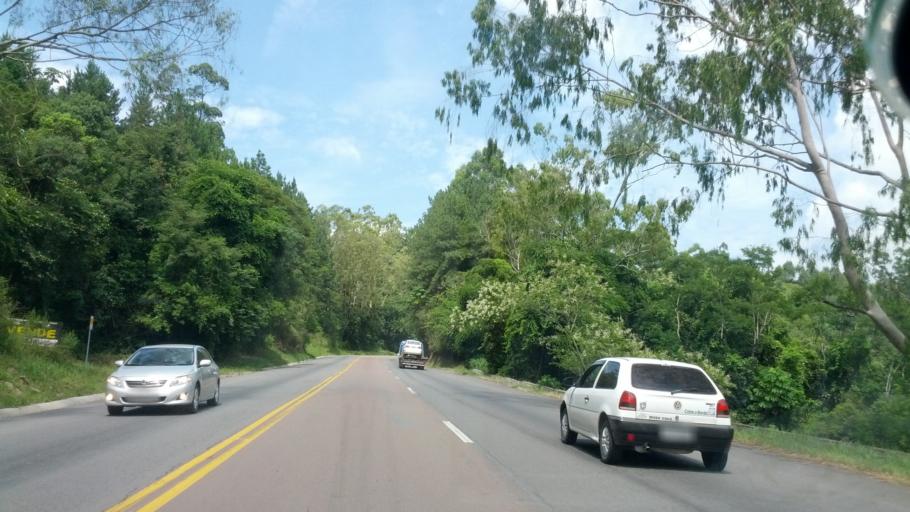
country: BR
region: Santa Catarina
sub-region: Ibirama
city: Ibirama
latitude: -27.0940
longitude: -49.5250
